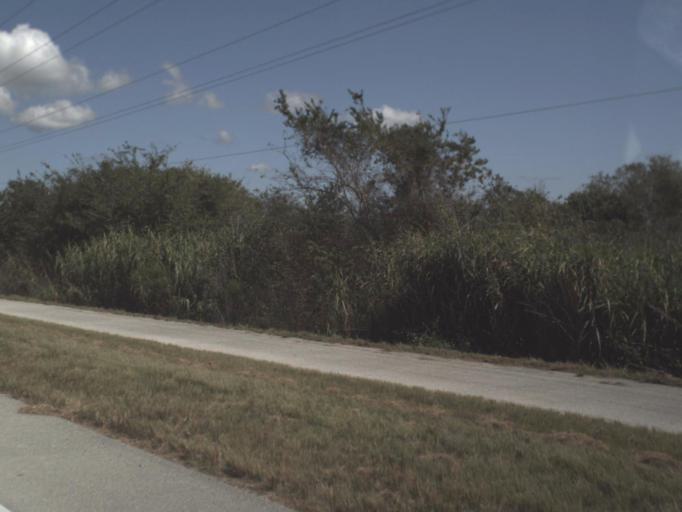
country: US
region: Florida
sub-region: Glades County
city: Moore Haven
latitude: 26.9386
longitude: -81.1222
